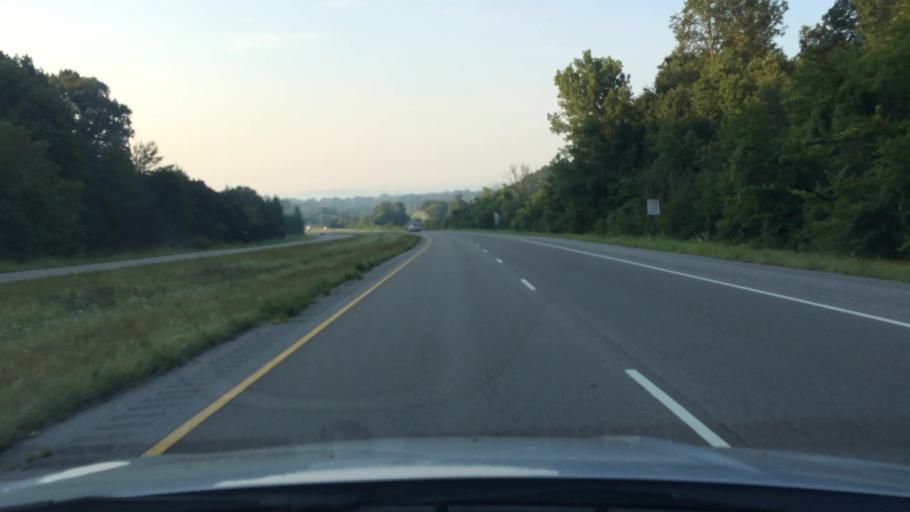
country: US
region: Tennessee
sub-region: Giles County
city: Pulaski
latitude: 35.1768
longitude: -87.0598
